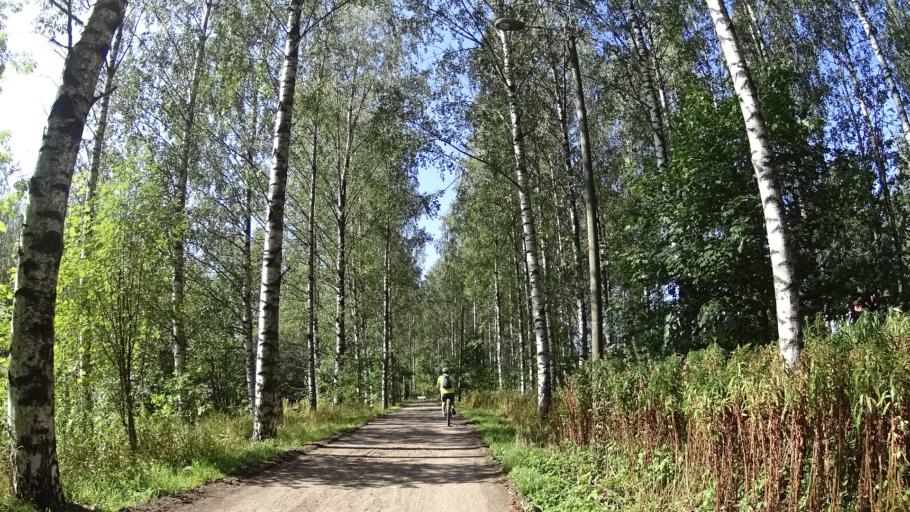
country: FI
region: Uusimaa
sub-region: Helsinki
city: Vantaa
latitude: 60.2429
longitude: 25.0017
